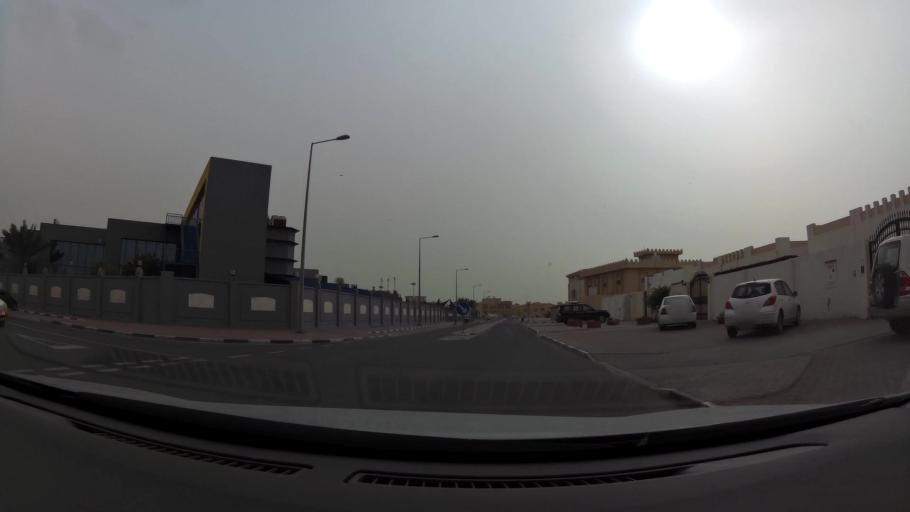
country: QA
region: Baladiyat ad Dawhah
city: Doha
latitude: 25.2454
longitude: 51.5107
